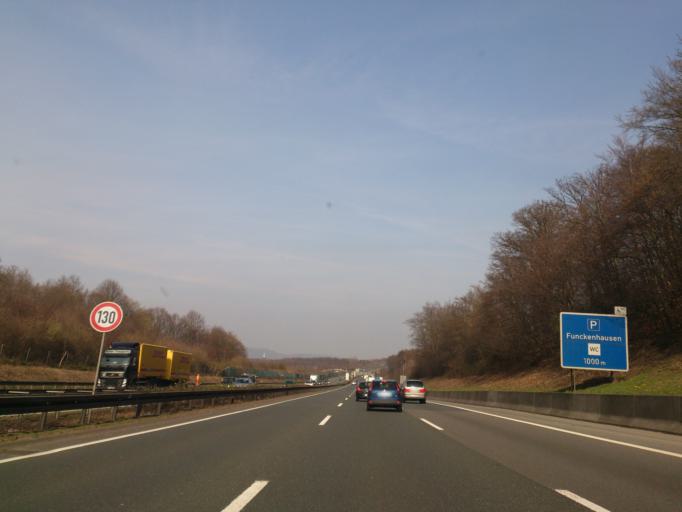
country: DE
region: North Rhine-Westphalia
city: Wetter (Ruhr)
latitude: 51.3668
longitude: 7.4037
